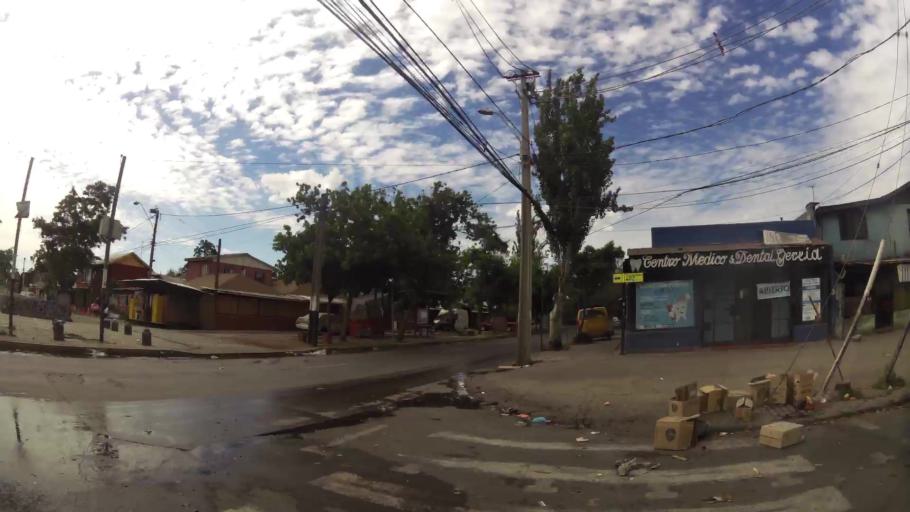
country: CL
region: Santiago Metropolitan
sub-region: Provincia de Santiago
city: La Pintana
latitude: -33.5807
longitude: -70.6386
